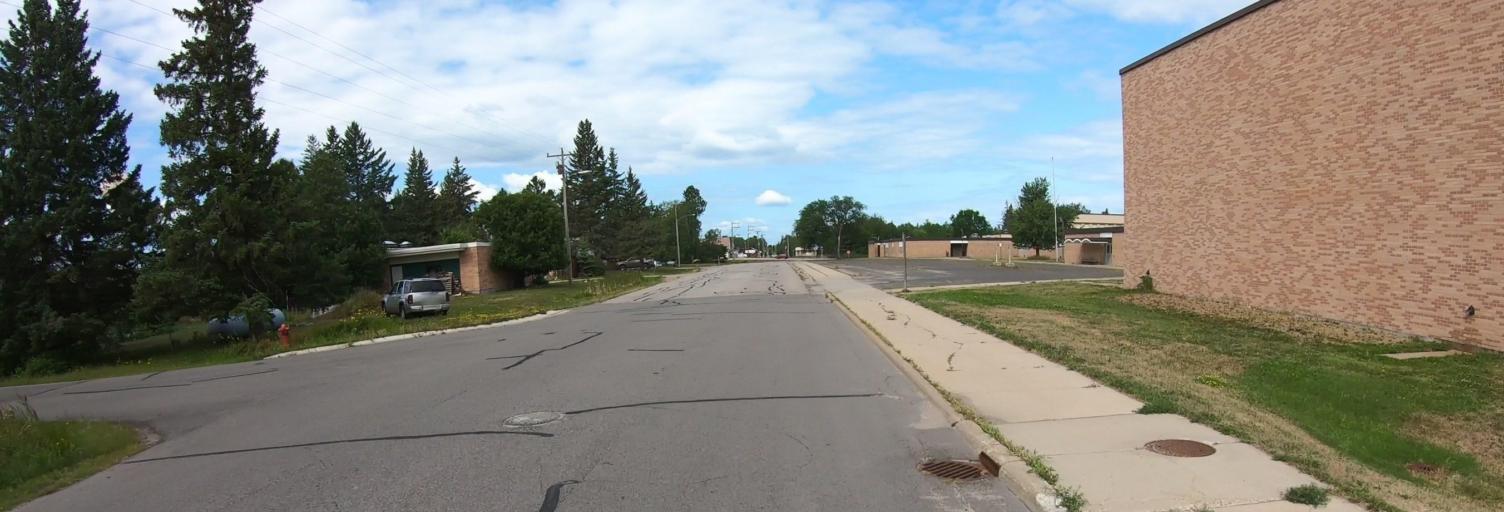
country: US
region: Minnesota
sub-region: Saint Louis County
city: Mountain Iron
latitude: 47.8539
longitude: -92.6822
